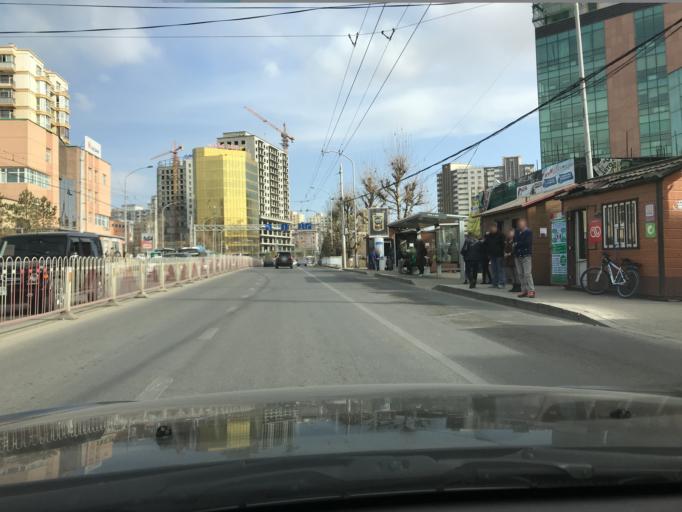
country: MN
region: Ulaanbaatar
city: Ulaanbaatar
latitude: 47.9188
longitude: 106.9403
